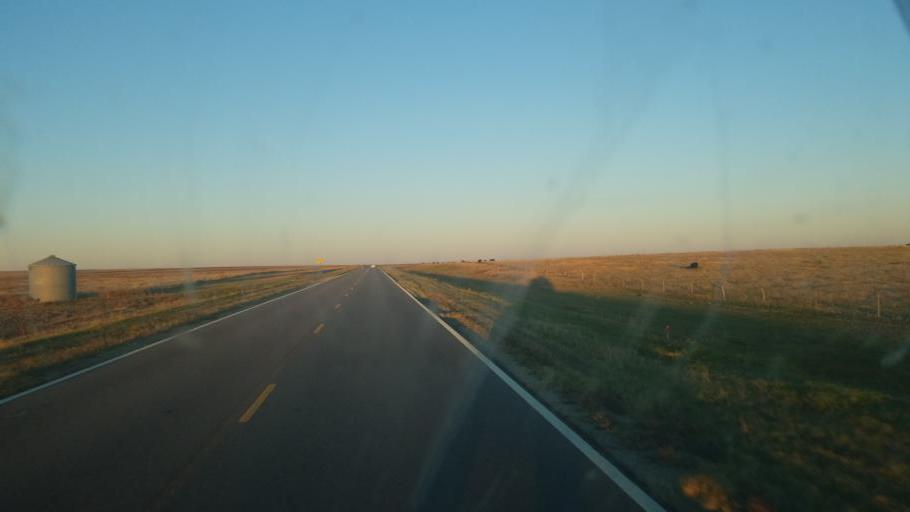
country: US
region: Kansas
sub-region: Wallace County
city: Sharon Springs
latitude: 38.9012
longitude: -101.8229
